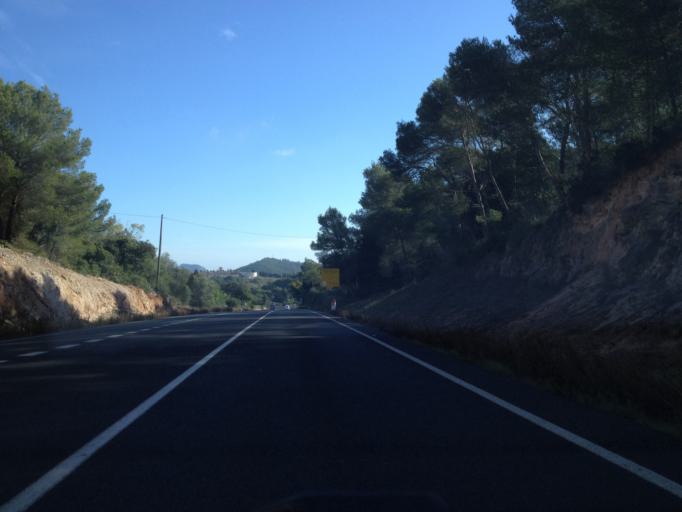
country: ES
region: Balearic Islands
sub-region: Illes Balears
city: Son Servera
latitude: 39.6213
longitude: 3.3421
